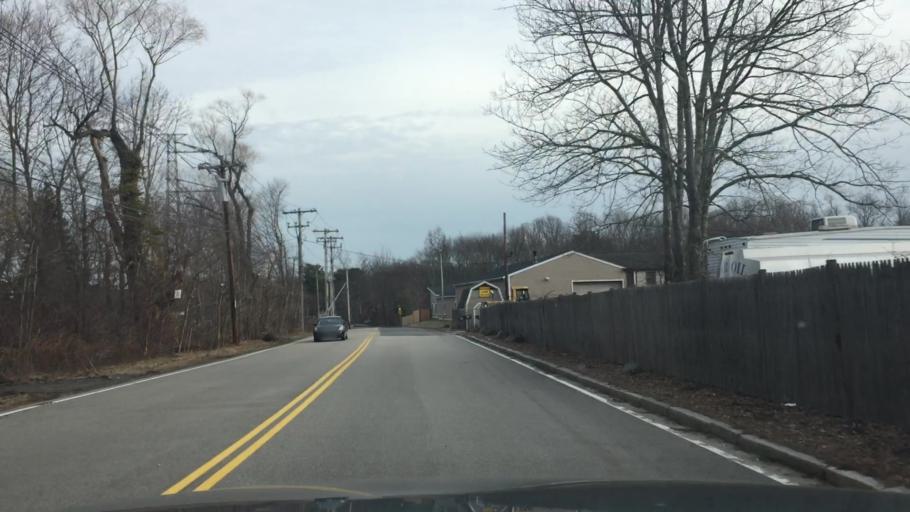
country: US
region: Massachusetts
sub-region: Norfolk County
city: Medway
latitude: 42.1370
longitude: -71.4495
